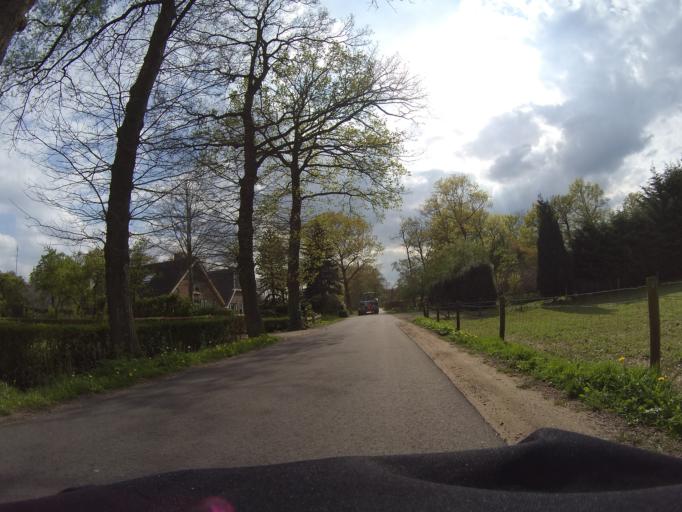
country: NL
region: Gelderland
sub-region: Gemeente Oldebroek
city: Oldebroek
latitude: 52.4412
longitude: 5.9067
